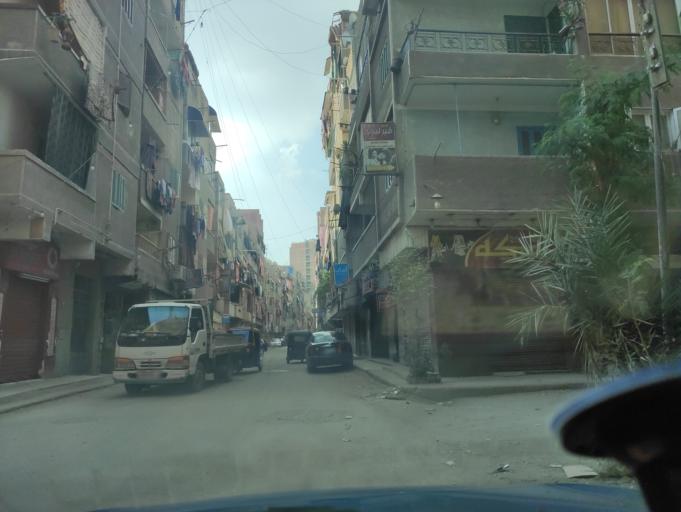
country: EG
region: Muhafazat al Qahirah
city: Cairo
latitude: 30.1240
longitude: 31.3061
